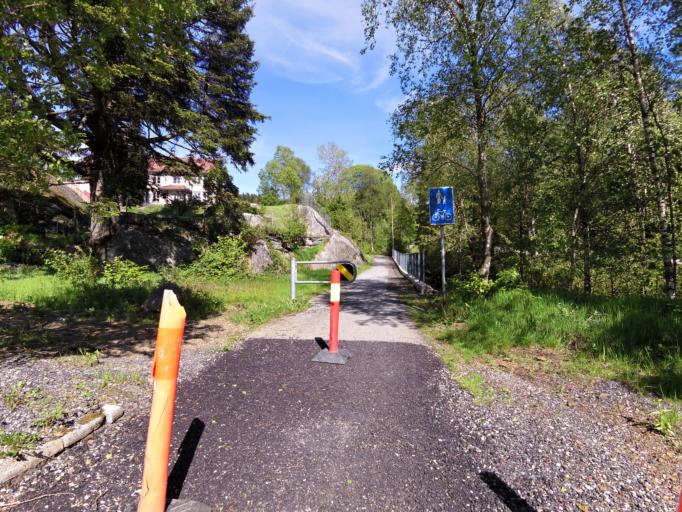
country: NO
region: Hordaland
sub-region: Stord
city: Sagvag
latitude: 59.7885
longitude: 5.4179
